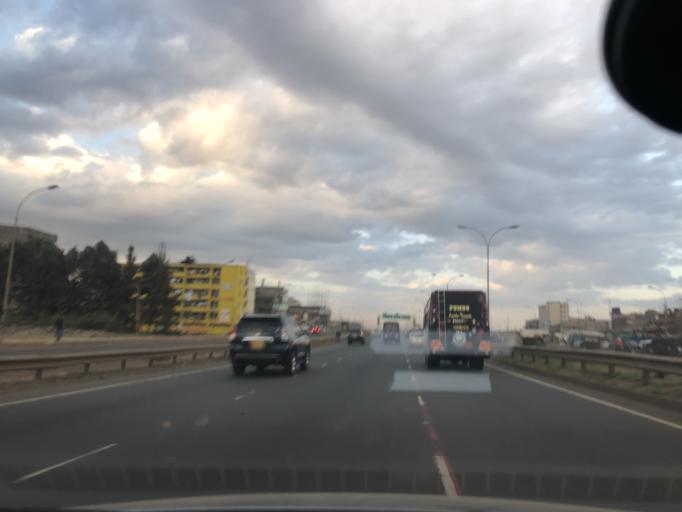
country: KE
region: Kiambu
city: Kiambu
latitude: -1.2083
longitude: 36.9125
